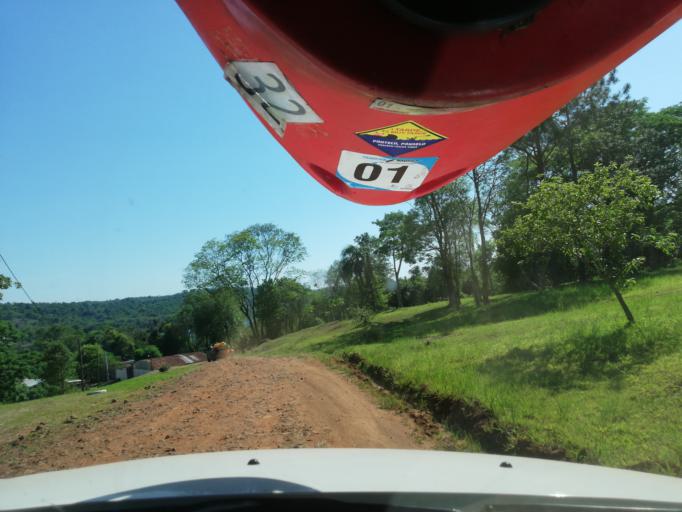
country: AR
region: Misiones
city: Puerto Leoni
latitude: -26.9606
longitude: -55.1525
